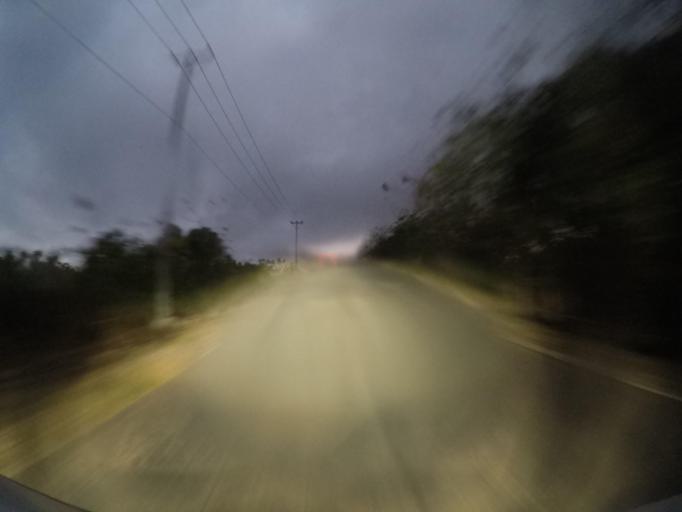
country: TL
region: Lautem
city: Lospalos
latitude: -8.4193
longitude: 127.0049
